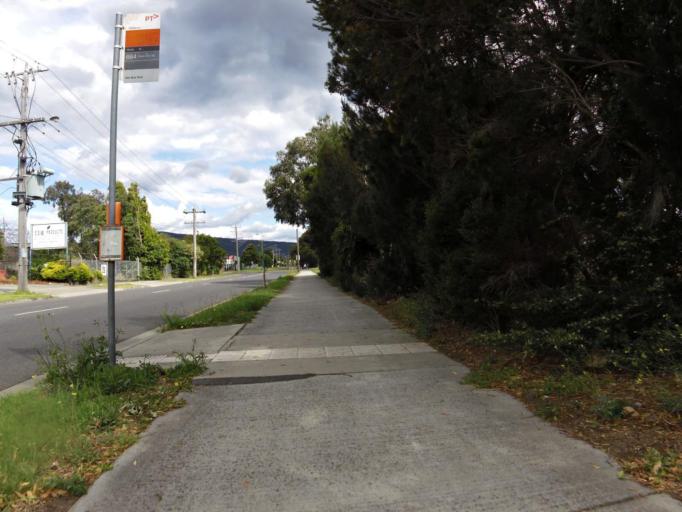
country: AU
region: Victoria
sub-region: Knox
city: Bayswater
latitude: -37.8460
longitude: 145.2726
